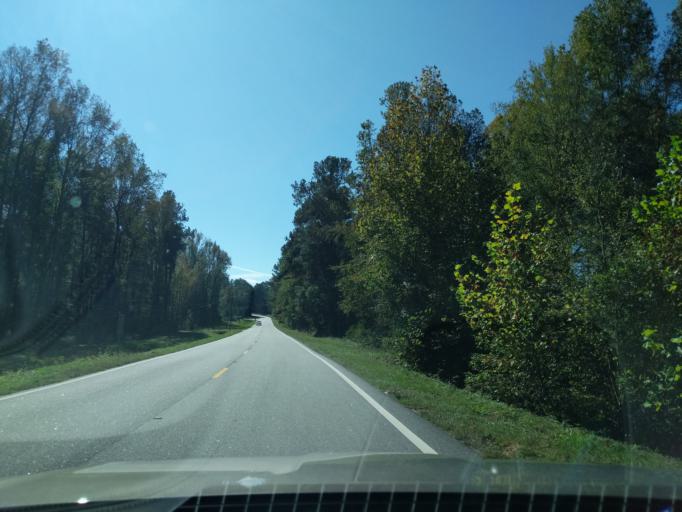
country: US
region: Georgia
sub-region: Richmond County
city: Hephzibah
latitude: 33.2910
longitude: -82.0227
